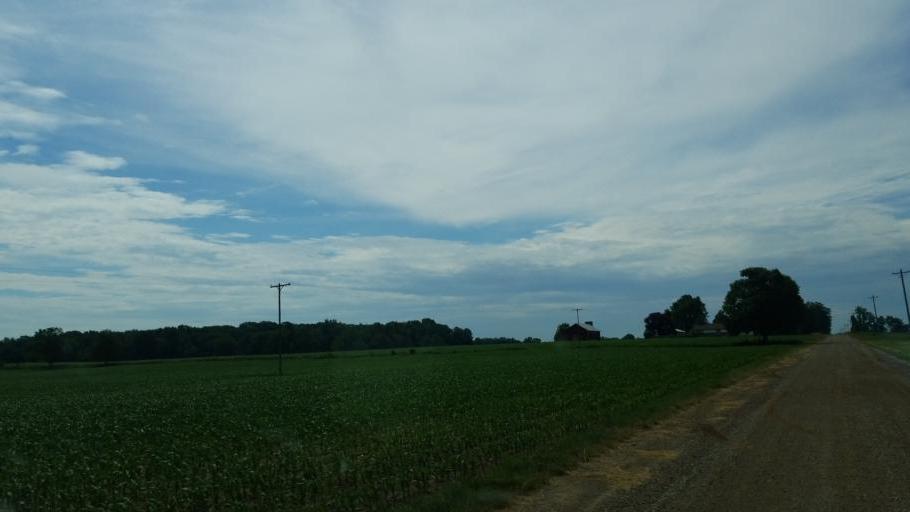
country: US
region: Michigan
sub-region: Eaton County
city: Charlotte
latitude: 42.6091
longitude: -84.8175
